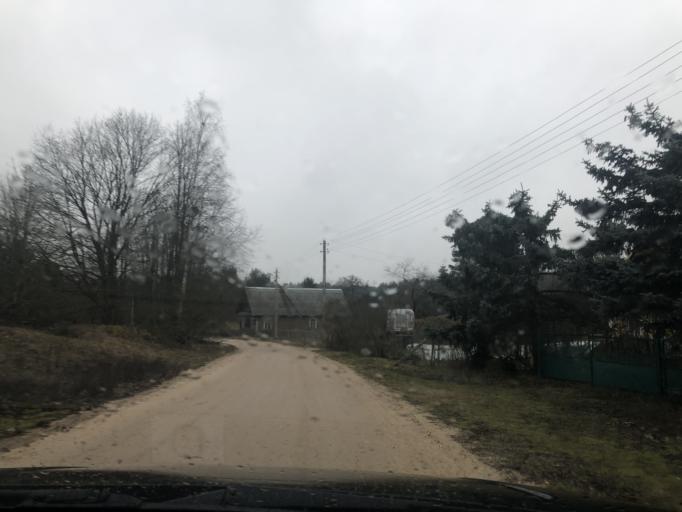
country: BY
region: Grodnenskaya
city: Skidal'
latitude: 53.8605
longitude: 24.2429
